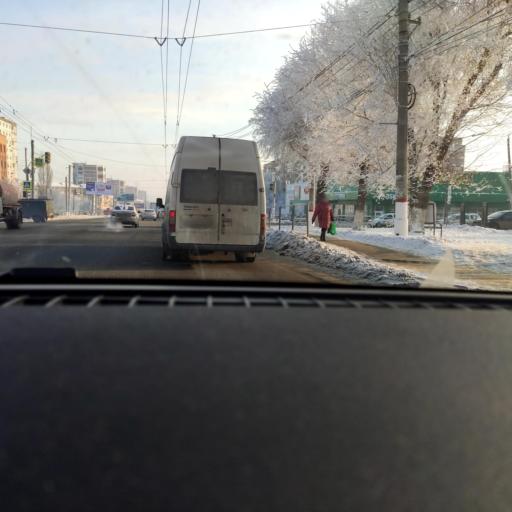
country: RU
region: Samara
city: Novokuybyshevsk
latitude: 53.0936
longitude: 49.9782
